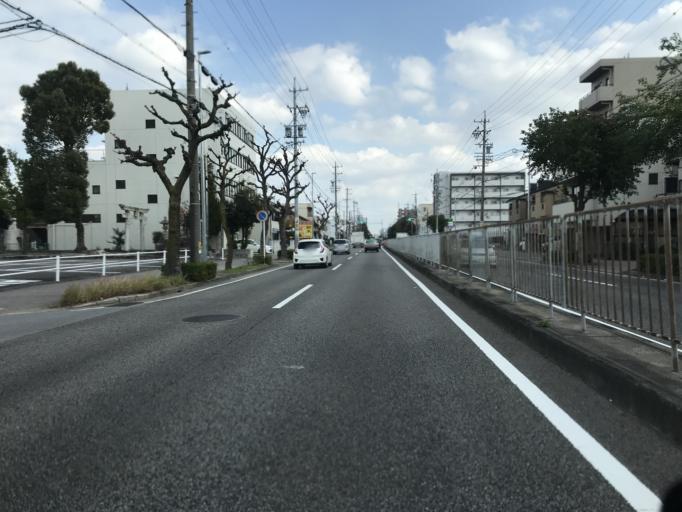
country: JP
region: Aichi
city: Nagoya-shi
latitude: 35.1777
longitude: 136.8544
